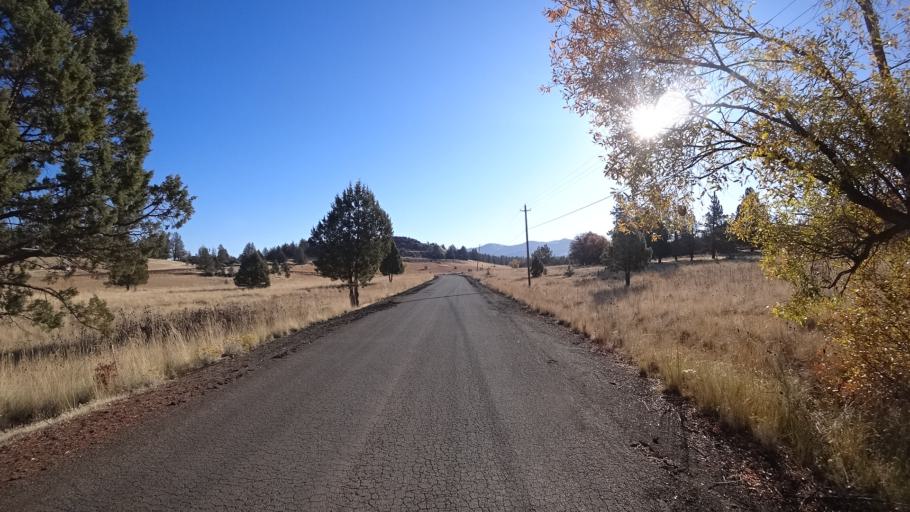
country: US
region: California
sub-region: Siskiyou County
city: Montague
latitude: 41.8805
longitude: -122.4506
